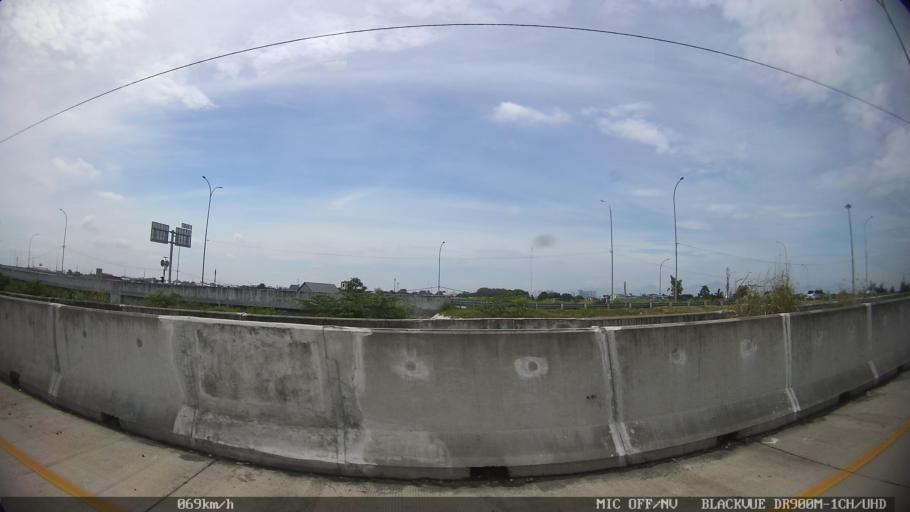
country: ID
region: North Sumatra
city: Medan
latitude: 3.6488
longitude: 98.6782
